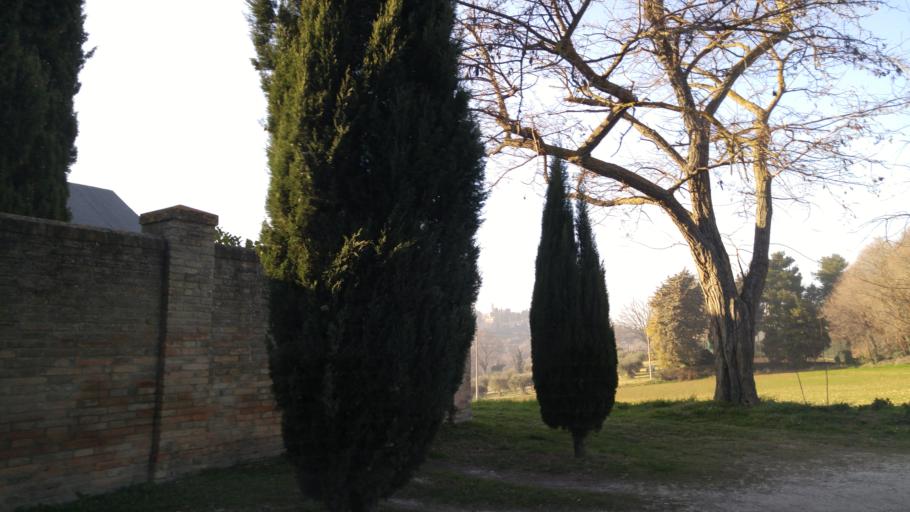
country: IT
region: The Marches
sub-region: Provincia di Pesaro e Urbino
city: Fenile
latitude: 43.8586
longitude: 12.9582
